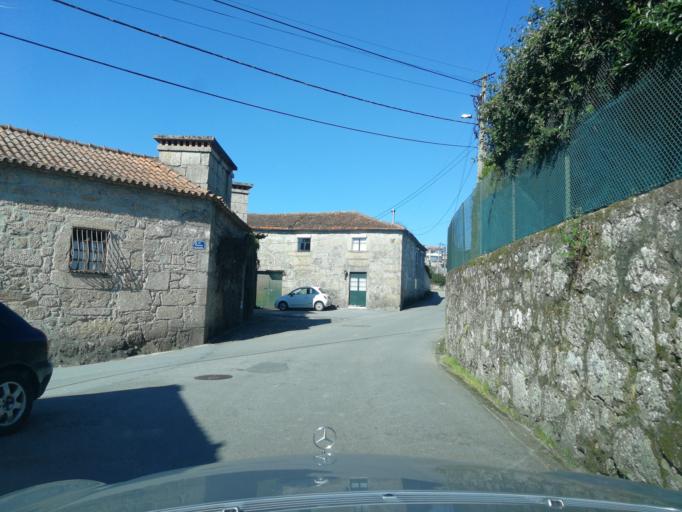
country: PT
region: Braga
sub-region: Vila Nova de Famalicao
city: Calendario
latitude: 41.3960
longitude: -8.5265
